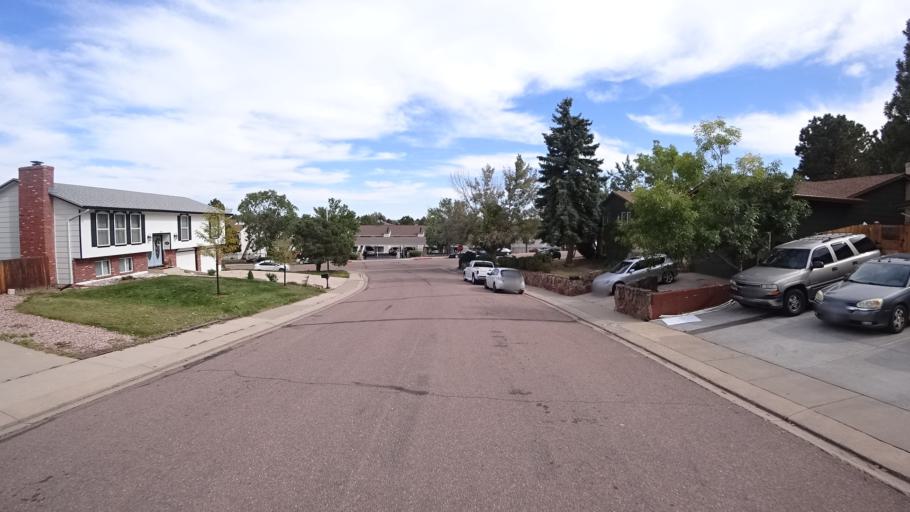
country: US
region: Colorado
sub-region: El Paso County
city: Colorado Springs
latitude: 38.9016
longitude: -104.7808
